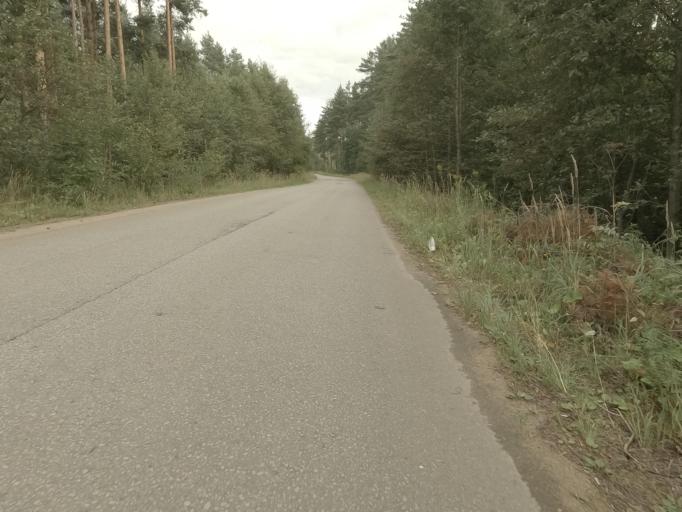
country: RU
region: Leningrad
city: Mga
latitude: 59.7602
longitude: 31.0230
